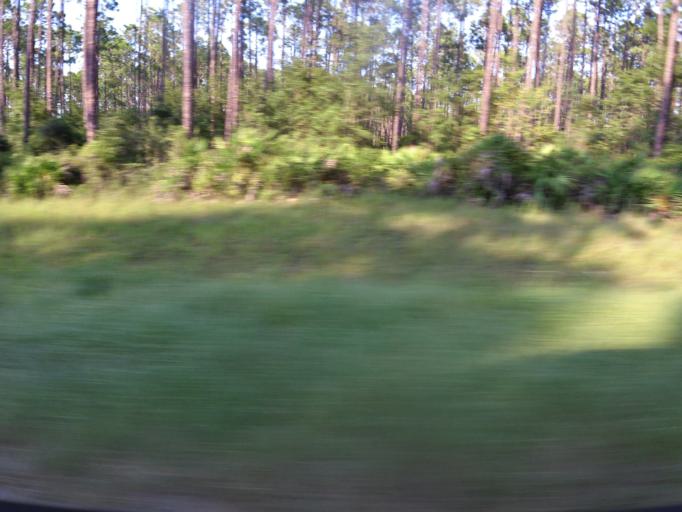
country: US
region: Florida
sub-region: Duval County
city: Baldwin
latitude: 30.3877
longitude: -82.0244
